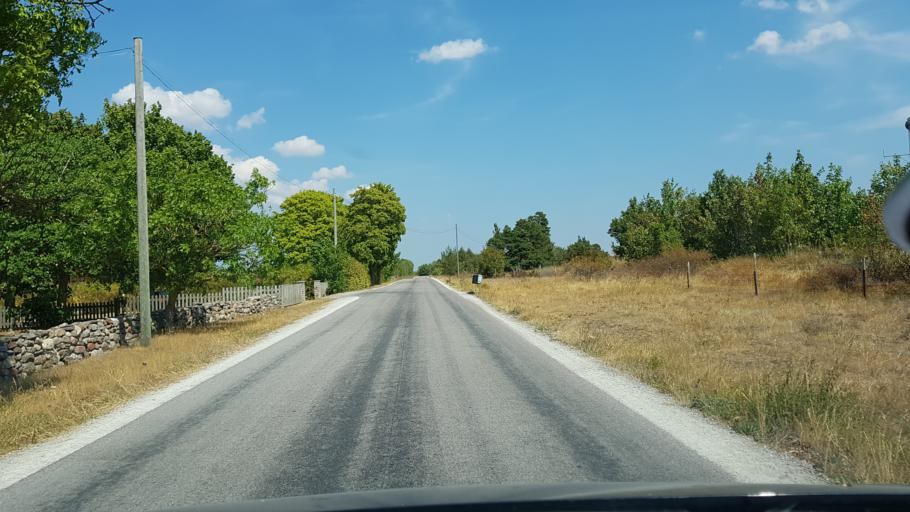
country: SE
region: Gotland
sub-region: Gotland
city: Visby
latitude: 57.6536
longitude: 18.3570
